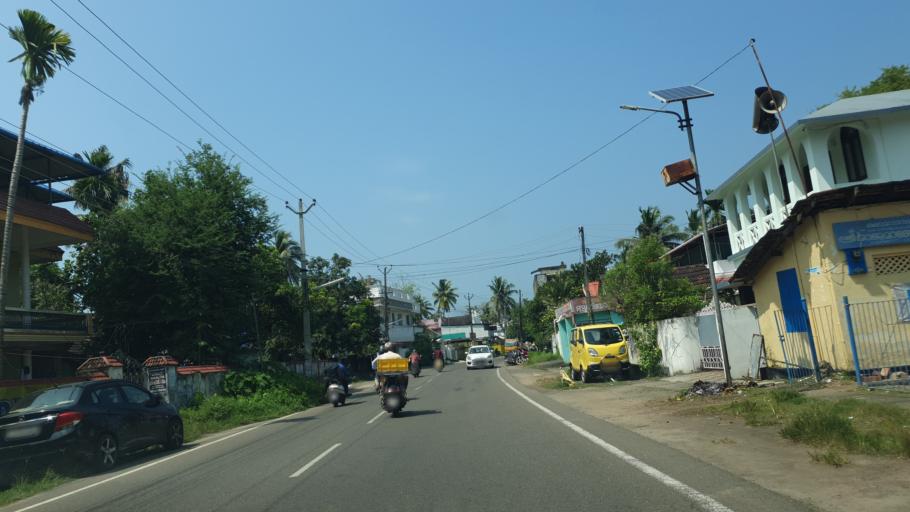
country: IN
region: Kerala
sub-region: Ernakulam
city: Cochin
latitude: 9.9759
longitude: 76.2419
